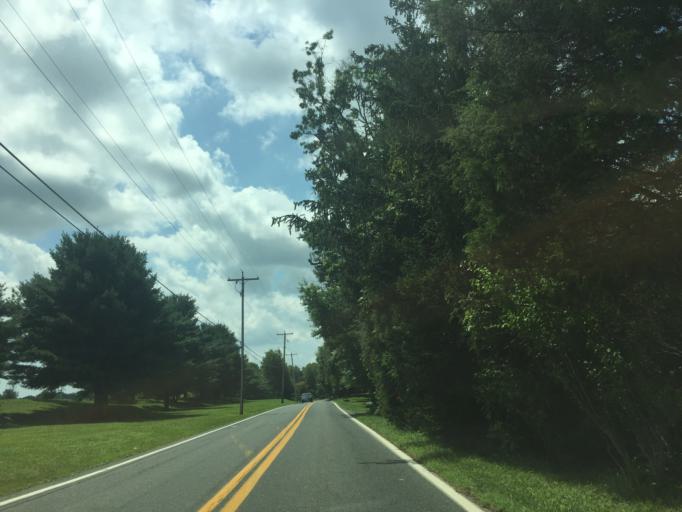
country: US
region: Maryland
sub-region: Baltimore County
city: Kingsville
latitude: 39.4248
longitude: -76.4077
